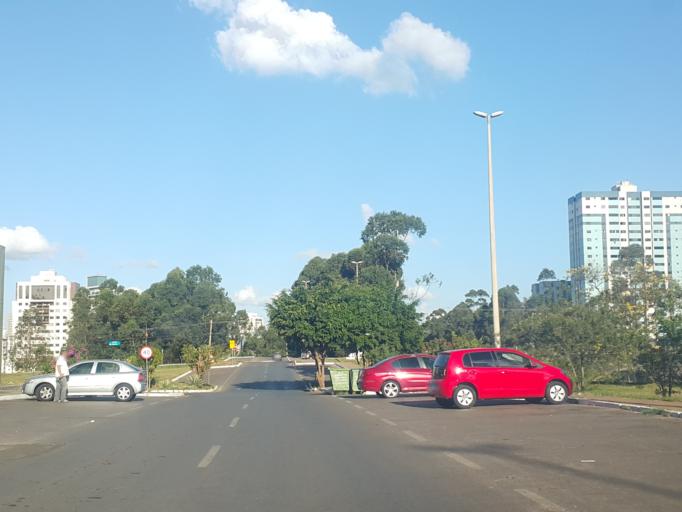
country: BR
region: Federal District
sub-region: Brasilia
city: Brasilia
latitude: -15.8364
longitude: -48.0364
